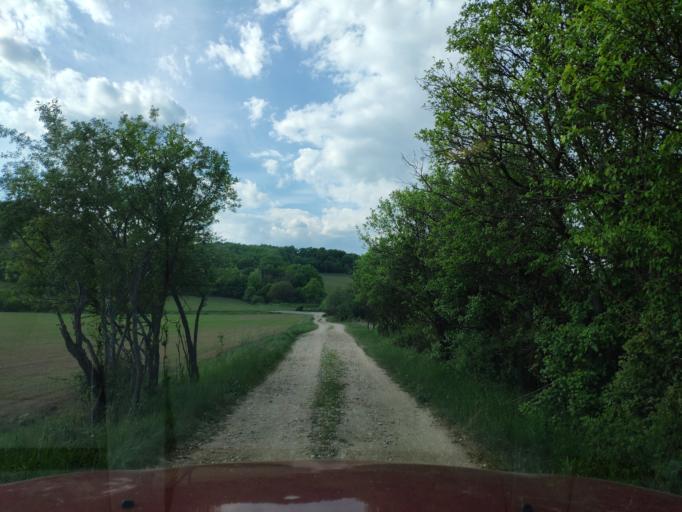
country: SK
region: Kosicky
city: Roznava
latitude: 48.5611
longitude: 20.6279
